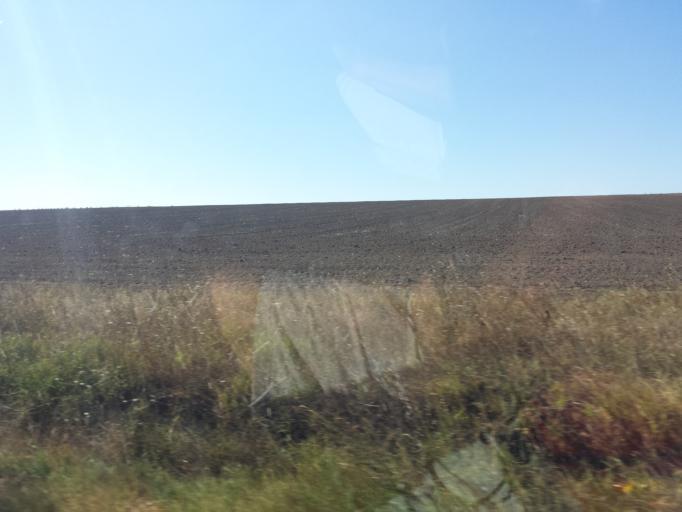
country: RO
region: Tulcea
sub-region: Comuna Frecatei
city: Cataloi
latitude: 45.1254
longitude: 28.7530
